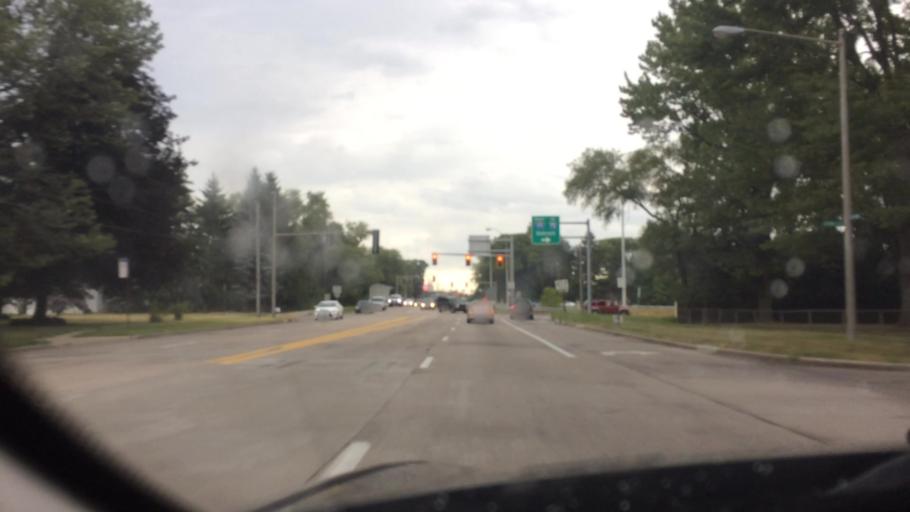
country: US
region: Ohio
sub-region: Lucas County
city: Ottawa Hills
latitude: 41.6867
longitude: -83.6444
